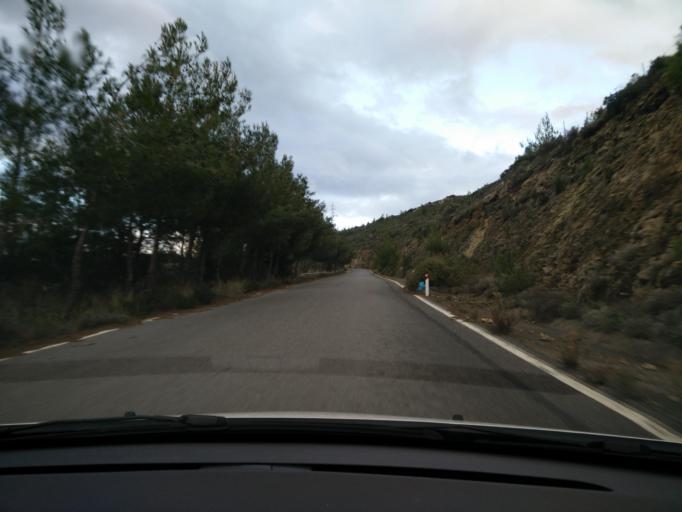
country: GR
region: Crete
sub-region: Nomos Lasithiou
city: Gra Liyia
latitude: 35.0896
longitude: 25.6981
